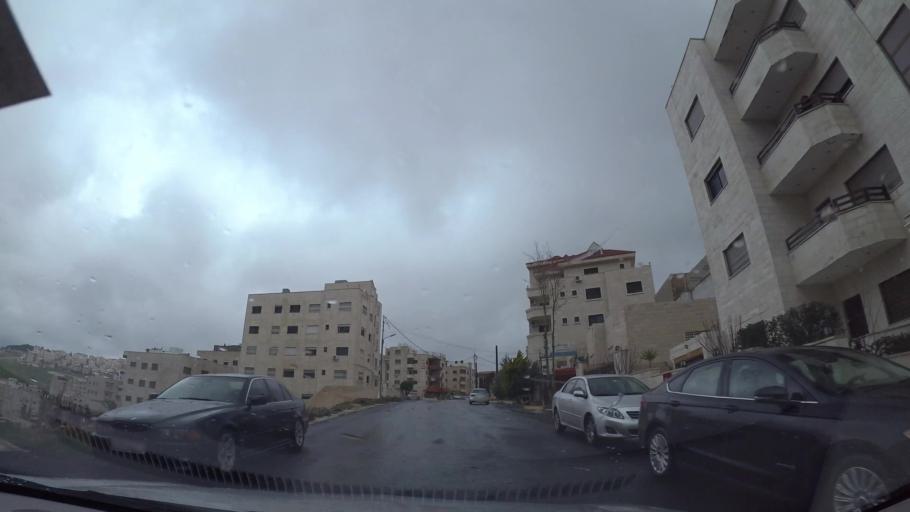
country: JO
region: Amman
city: Al Jubayhah
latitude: 32.0432
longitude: 35.8868
